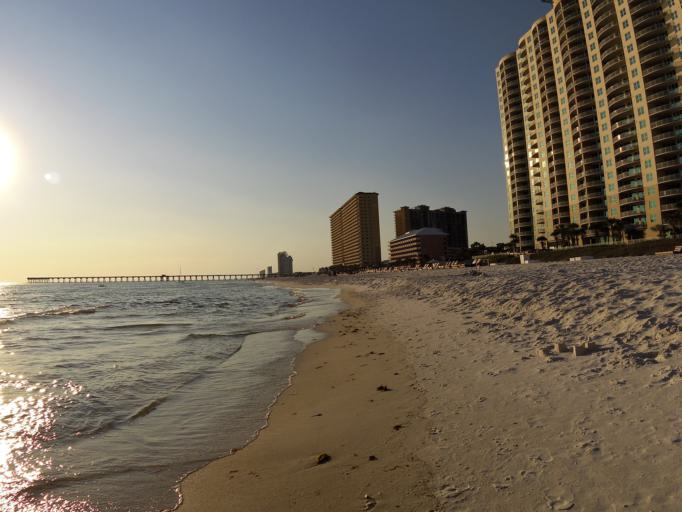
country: US
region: Florida
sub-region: Bay County
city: Laguna Beach
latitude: 30.2111
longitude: -85.8705
